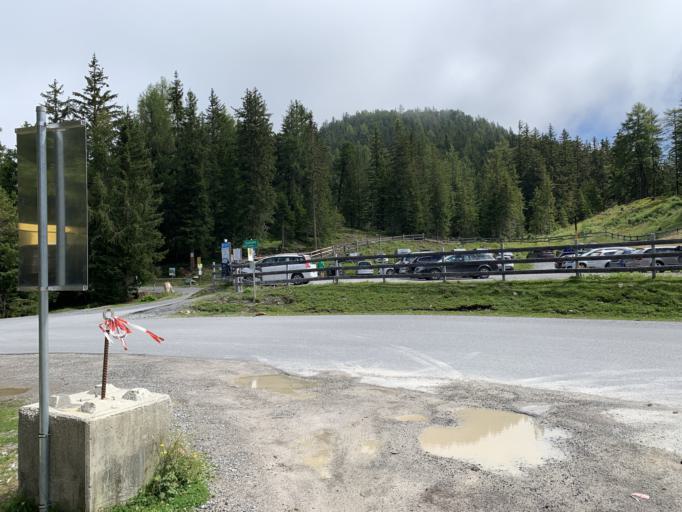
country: AT
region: Tyrol
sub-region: Politischer Bezirk Imst
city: Silz
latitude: 47.2312
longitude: 10.9276
